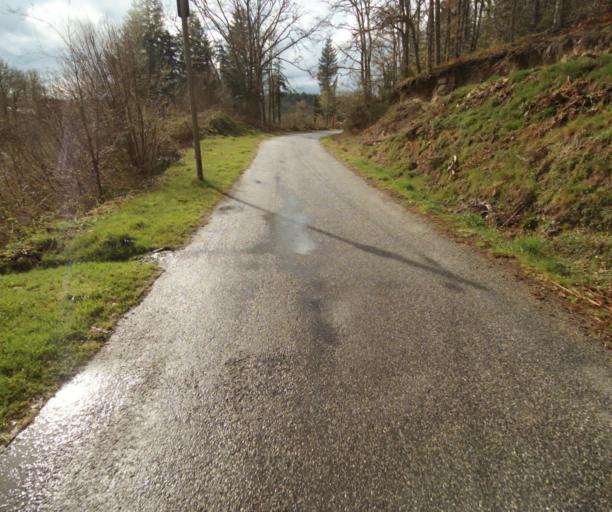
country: FR
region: Limousin
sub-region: Departement de la Correze
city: Saint-Privat
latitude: 45.2487
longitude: 1.9933
